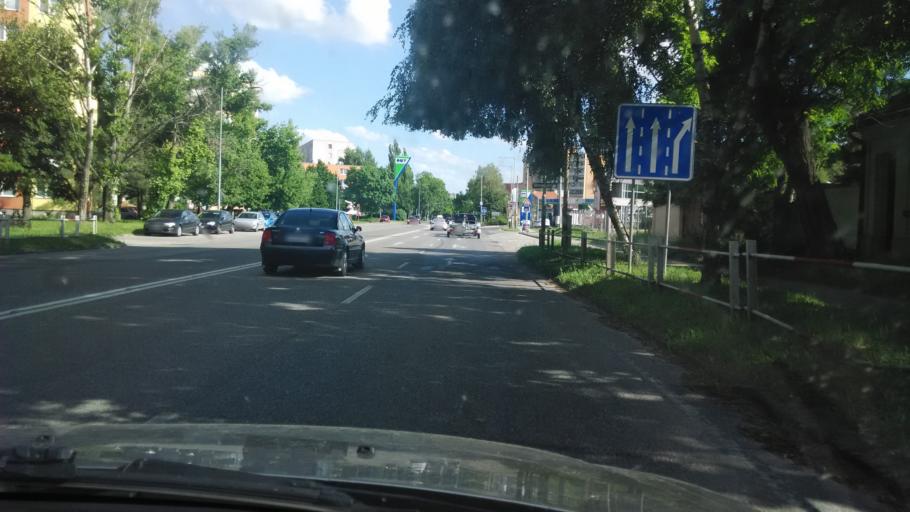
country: SK
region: Nitriansky
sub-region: Okres Nove Zamky
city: Nove Zamky
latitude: 47.9951
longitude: 18.1668
